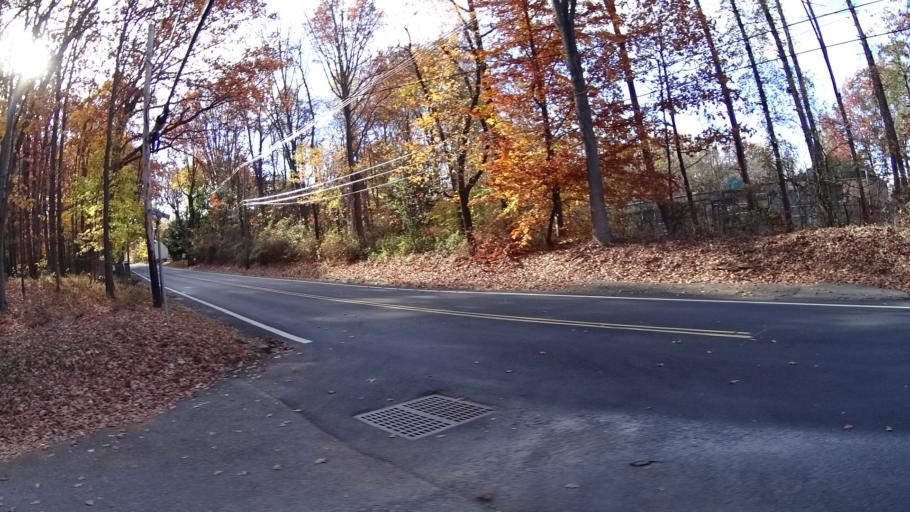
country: US
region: New Jersey
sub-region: Morris County
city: Morristown
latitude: 40.7410
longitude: -74.5019
